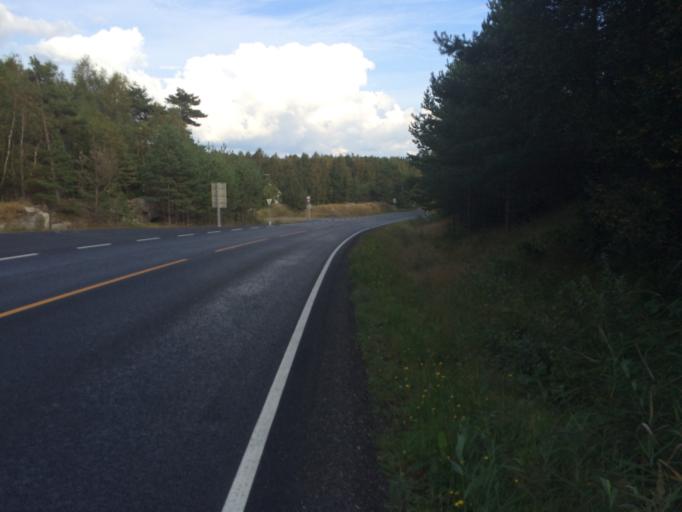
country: NO
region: Ostfold
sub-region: Hvaler
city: Skjaerhalden
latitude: 59.0376
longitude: 11.0067
